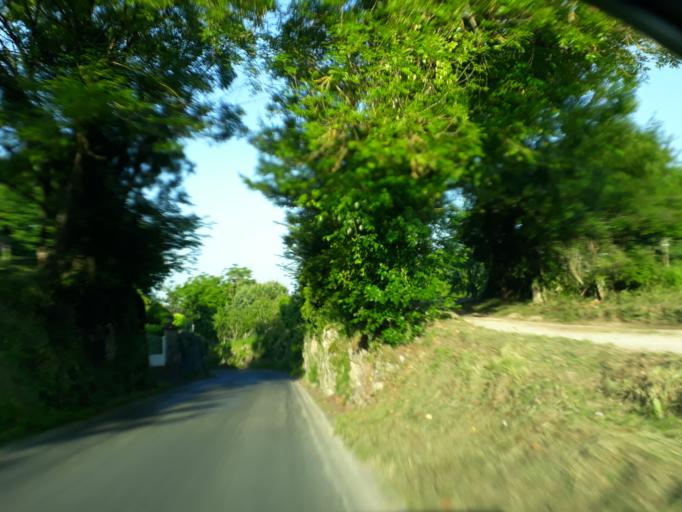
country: FR
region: Limousin
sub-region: Departement de la Correze
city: Saint-Pantaleon-de-Larche
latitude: 45.1048
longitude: 1.4641
